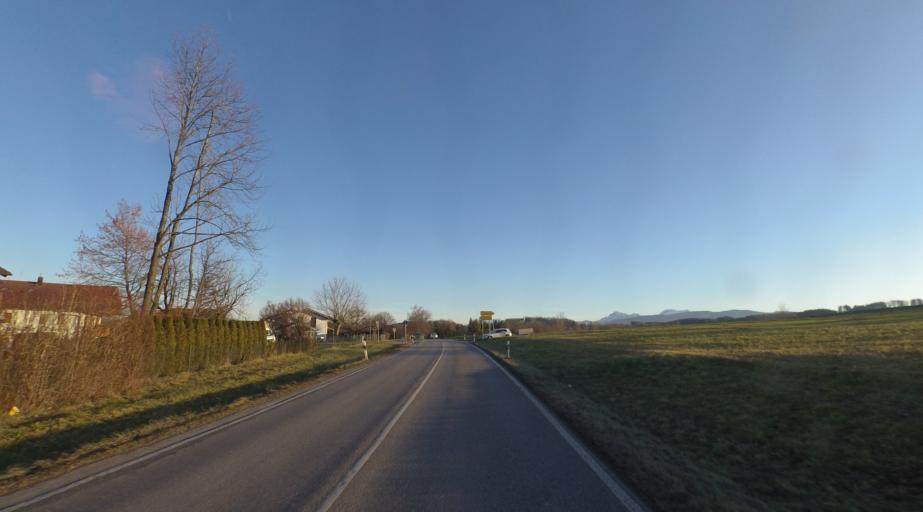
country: DE
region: Bavaria
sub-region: Upper Bavaria
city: Waging am See
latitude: 47.9425
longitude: 12.7376
